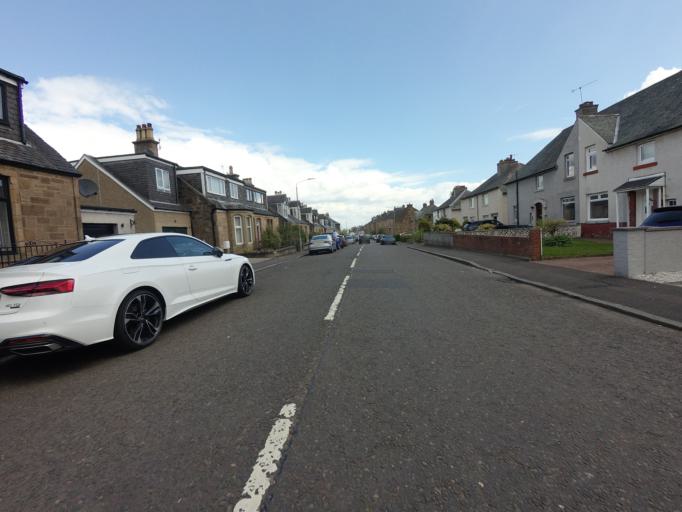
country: GB
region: Scotland
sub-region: Falkirk
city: Falkirk
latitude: 56.0114
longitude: -3.7939
